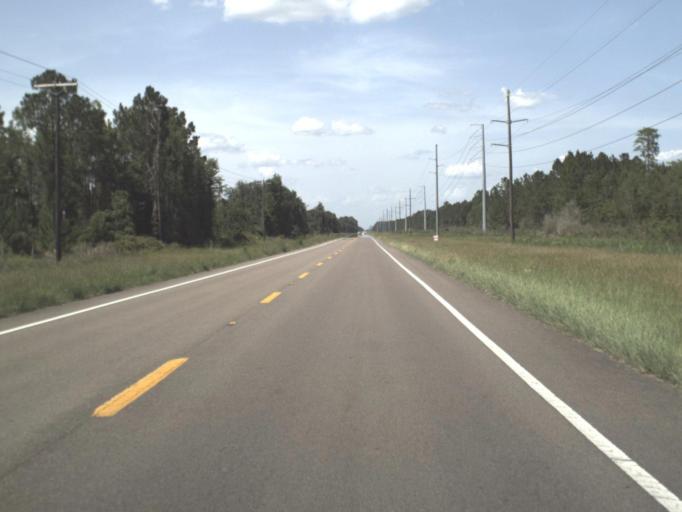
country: US
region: Florida
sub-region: Gilchrist County
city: Trenton
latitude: 29.6411
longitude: -82.7933
